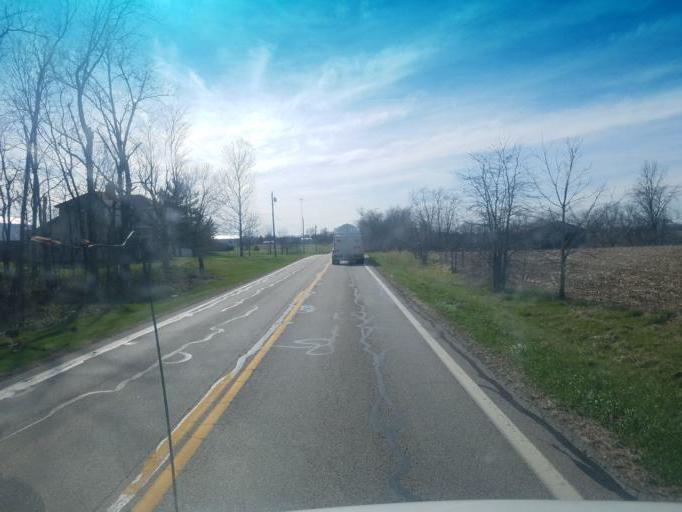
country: US
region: Ohio
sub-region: Union County
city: Richwood
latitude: 40.3458
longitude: -83.3118
